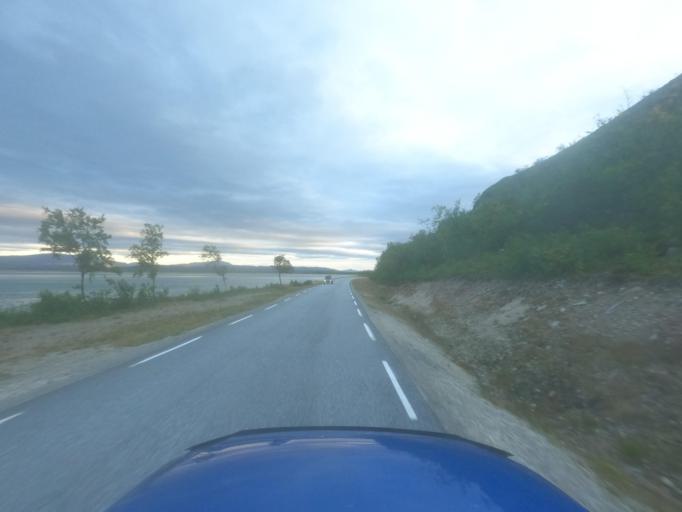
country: NO
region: Finnmark Fylke
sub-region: Porsanger
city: Lakselv
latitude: 70.0950
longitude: 24.9118
